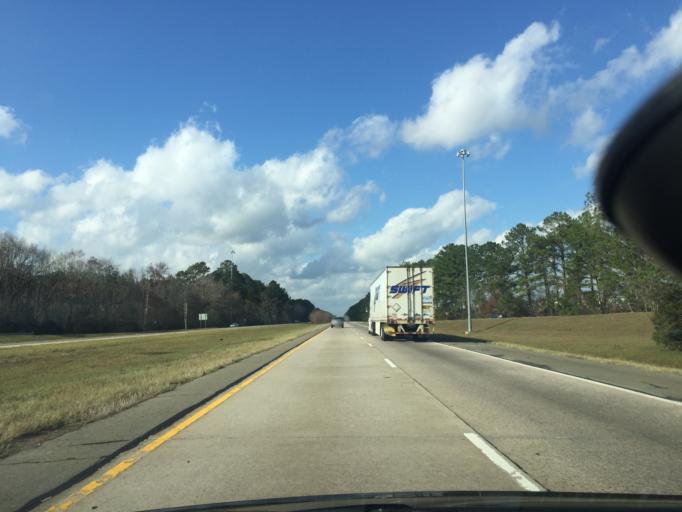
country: US
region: Georgia
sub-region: Bryan County
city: Pembroke
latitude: 32.1821
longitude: -81.4612
